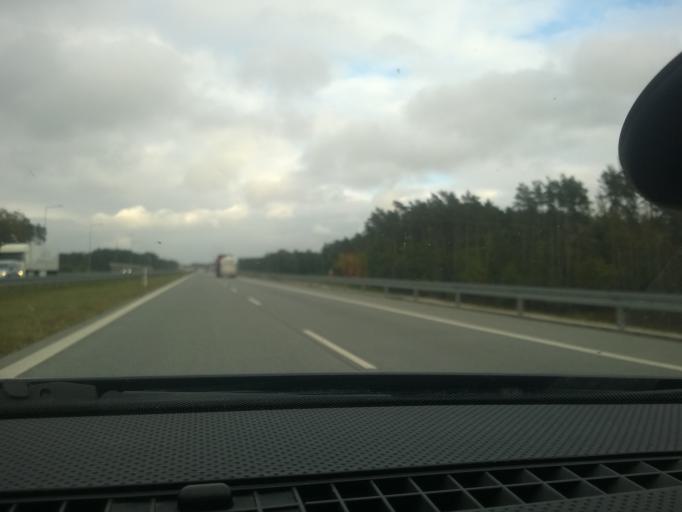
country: PL
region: Lodz Voivodeship
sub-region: Powiat pabianicki
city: Dobron
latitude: 51.5969
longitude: 19.2535
